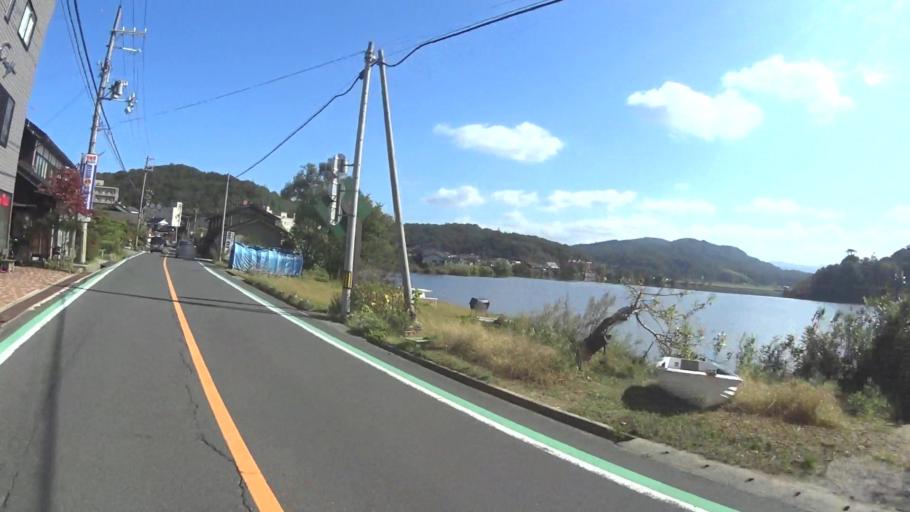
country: JP
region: Kyoto
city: Miyazu
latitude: 35.6922
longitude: 135.0358
